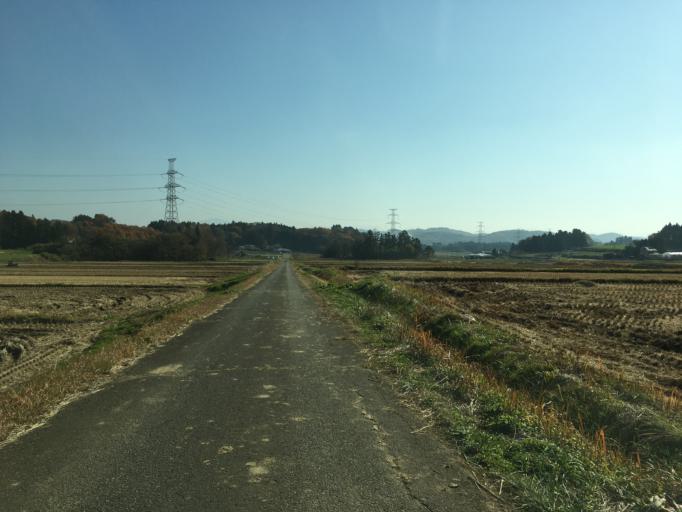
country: JP
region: Fukushima
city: Nihommatsu
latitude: 37.5720
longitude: 140.3779
